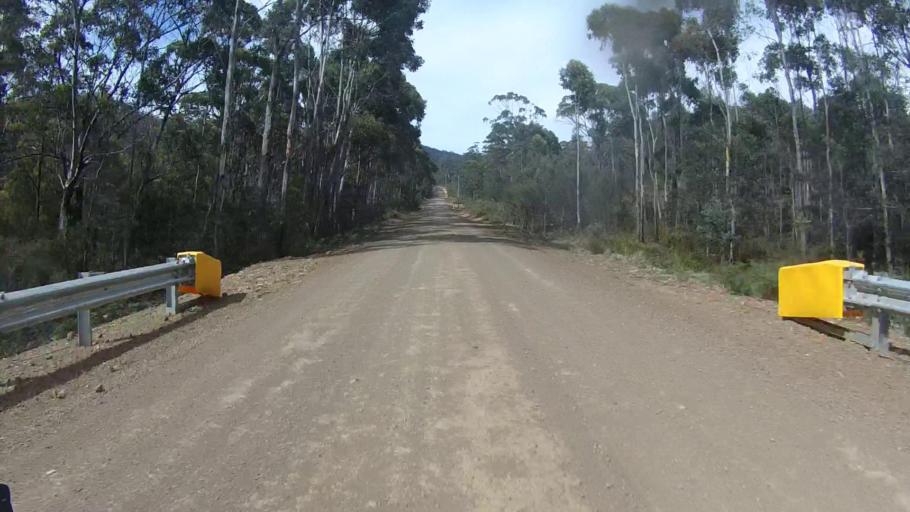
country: AU
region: Tasmania
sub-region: Sorell
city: Sorell
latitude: -42.6789
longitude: 147.8828
